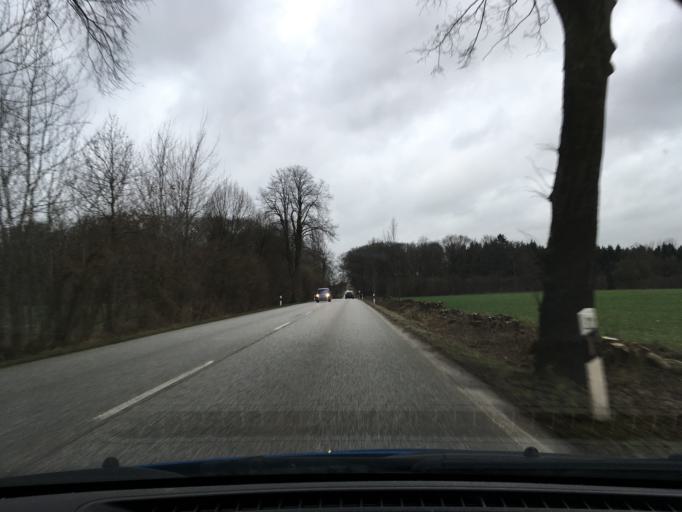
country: DE
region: Schleswig-Holstein
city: Schulendorf
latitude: 53.4777
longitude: 10.5315
